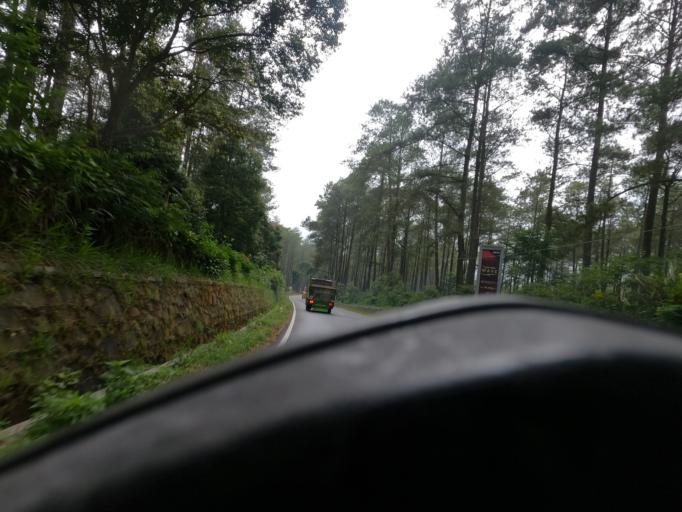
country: ID
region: West Java
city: Lembang
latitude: -6.7794
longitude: 107.6438
